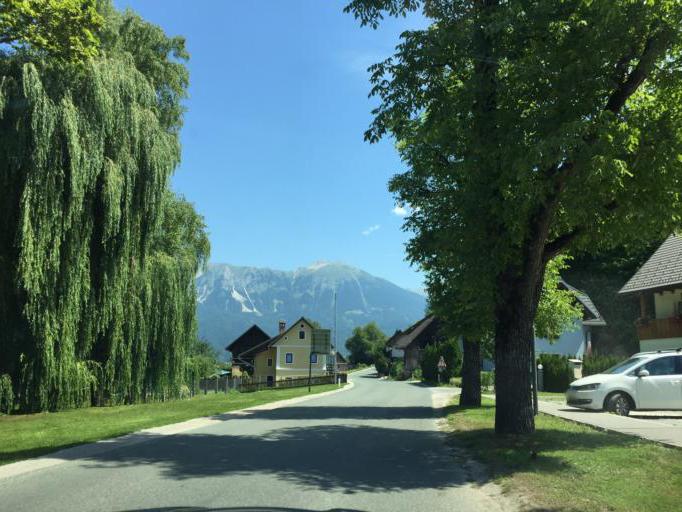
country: SI
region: Bled
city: Bled
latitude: 46.3727
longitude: 14.1011
